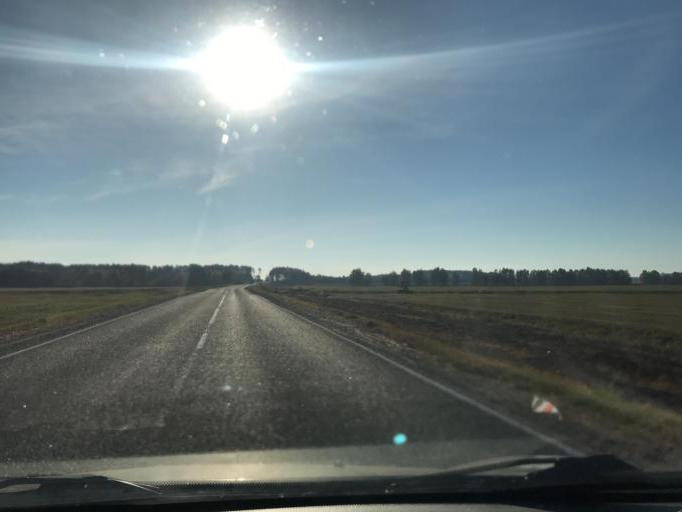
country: BY
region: Gomel
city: Brahin
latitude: 51.7738
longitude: 30.2926
